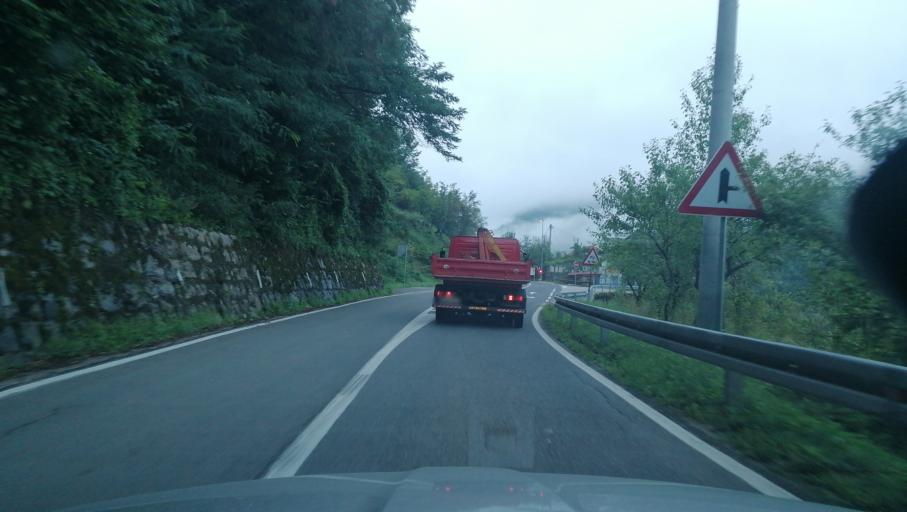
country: BA
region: Federation of Bosnia and Herzegovina
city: Jablanica
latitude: 43.7228
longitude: 17.7054
